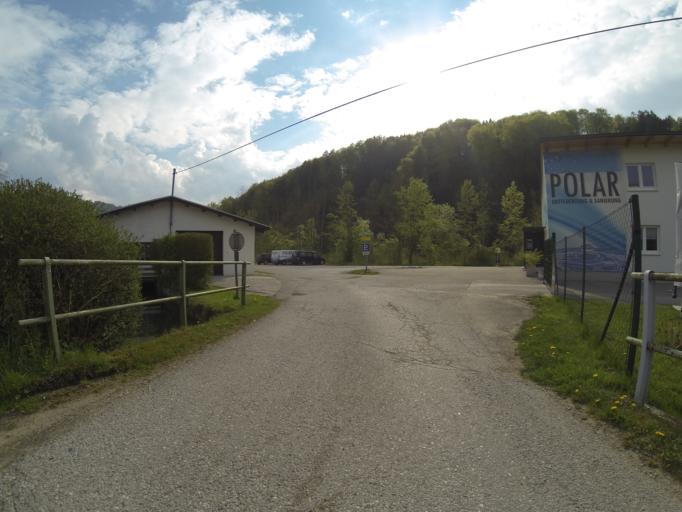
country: AT
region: Upper Austria
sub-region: Politischer Bezirk Gmunden
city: Altmunster
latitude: 47.9319
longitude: 13.7540
